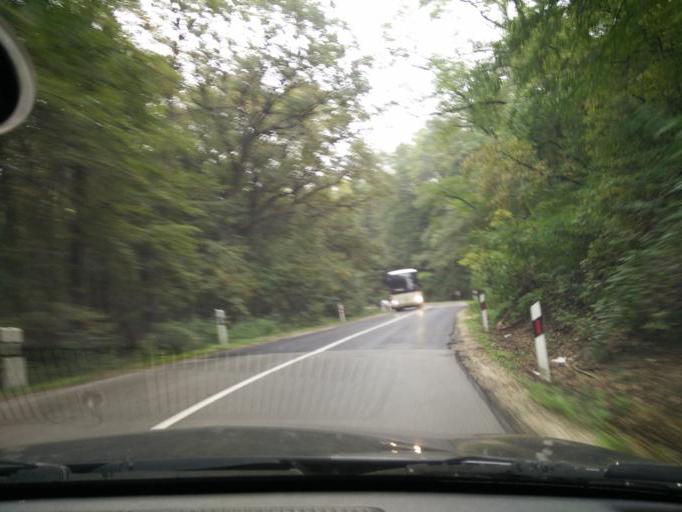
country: HU
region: Komarom-Esztergom
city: Tarjan
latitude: 47.5730
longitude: 18.4758
